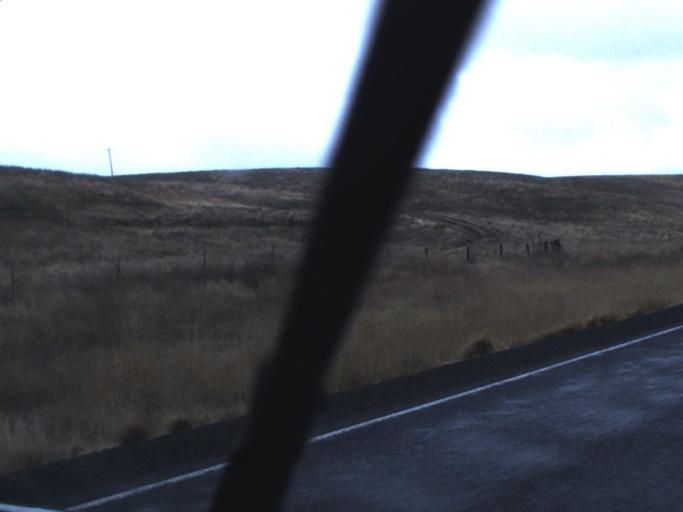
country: US
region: Washington
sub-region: Spokane County
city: Cheney
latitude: 47.1157
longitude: -117.7163
